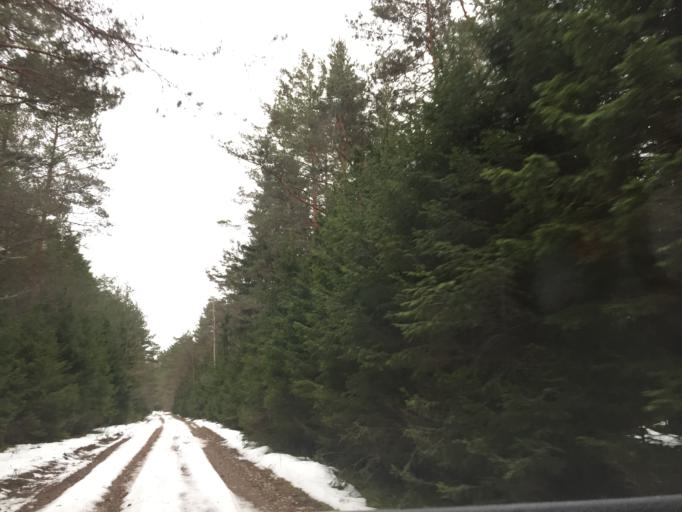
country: EE
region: Saare
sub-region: Kuressaare linn
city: Kuressaare
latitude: 58.4800
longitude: 22.2500
